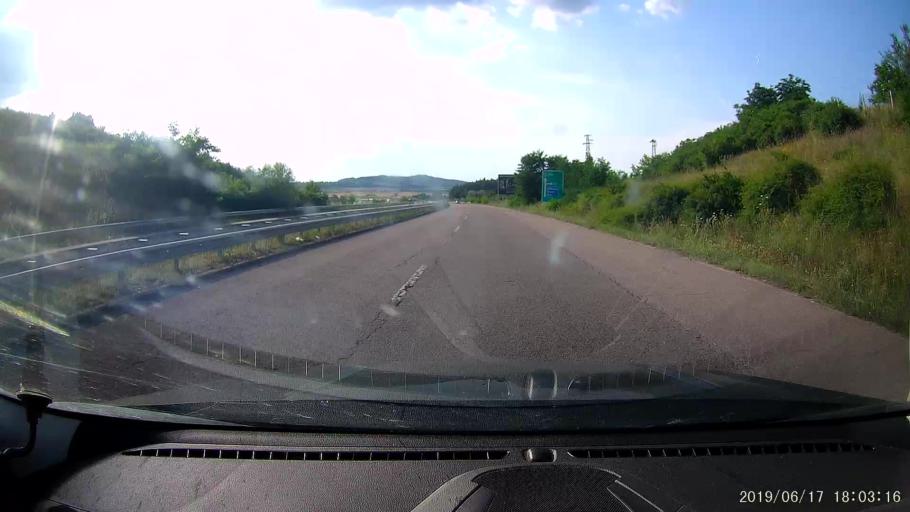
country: BG
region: Khaskovo
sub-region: Obshtina Svilengrad
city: Svilengrad
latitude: 41.7754
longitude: 26.2216
